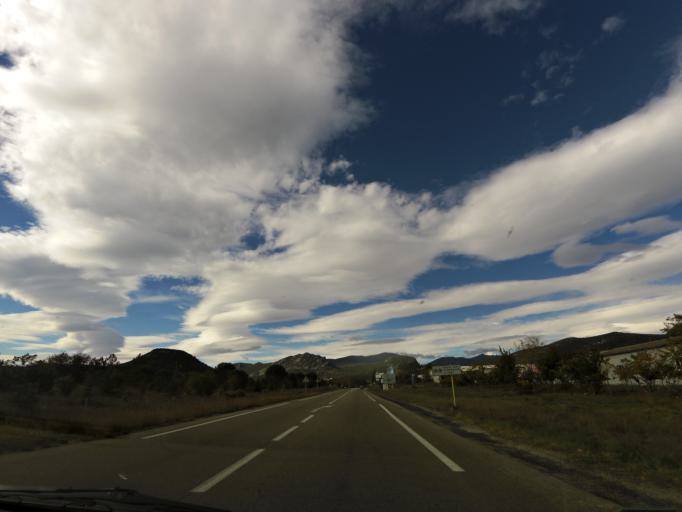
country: FR
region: Languedoc-Roussillon
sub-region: Departement du Gard
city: Saint-Hippolyte-du-Fort
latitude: 43.9525
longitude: 3.8784
